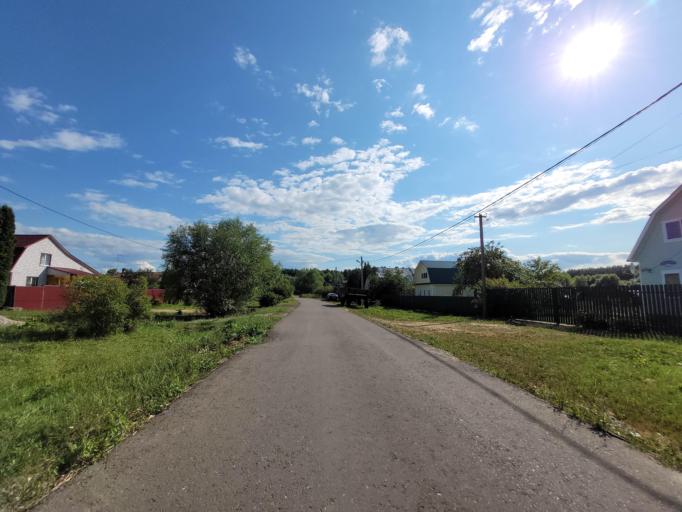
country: RU
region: Moskovskaya
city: Lopatinskiy
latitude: 55.3882
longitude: 38.7130
